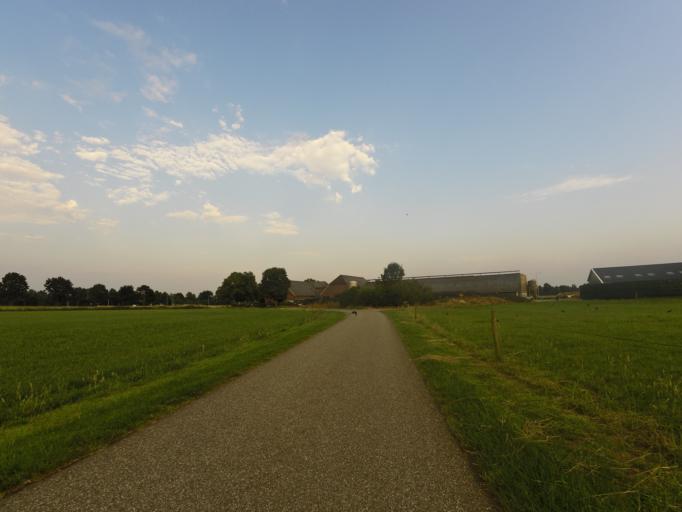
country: NL
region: Gelderland
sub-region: Oude IJsselstreek
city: Gendringen
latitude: 51.8812
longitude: 6.3653
